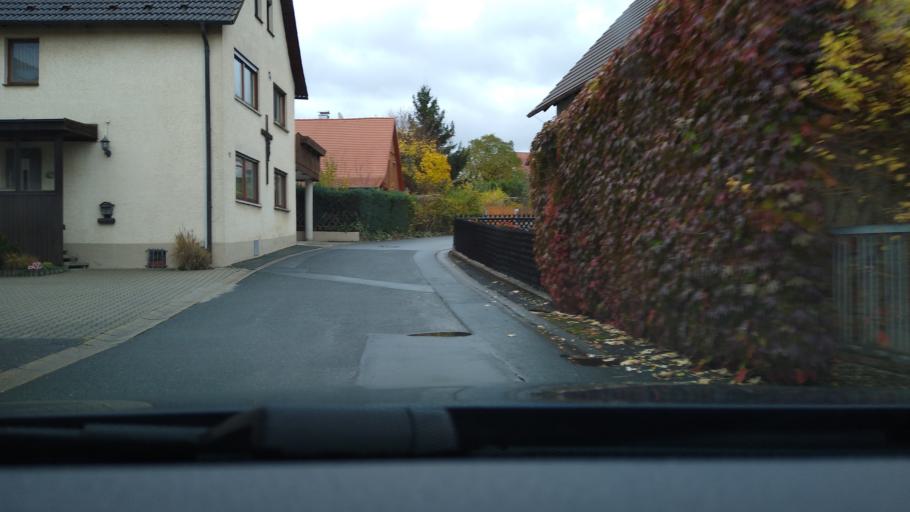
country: DE
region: Bavaria
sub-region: Regierungsbezirk Mittelfranken
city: Hemhofen
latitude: 49.6952
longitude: 10.9302
